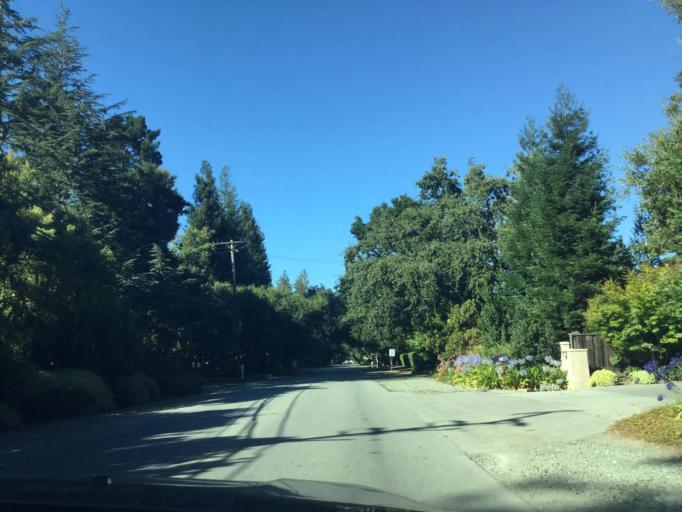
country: US
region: California
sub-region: San Mateo County
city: Atherton
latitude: 37.4635
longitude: -122.2147
